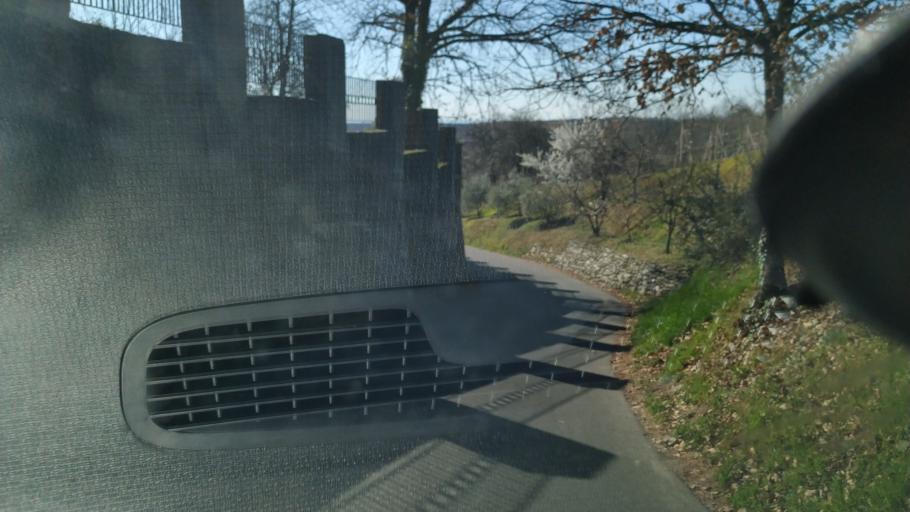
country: IT
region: Piedmont
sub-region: Provincia di Vercelli
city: Gattinara
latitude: 45.6210
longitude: 8.3652
